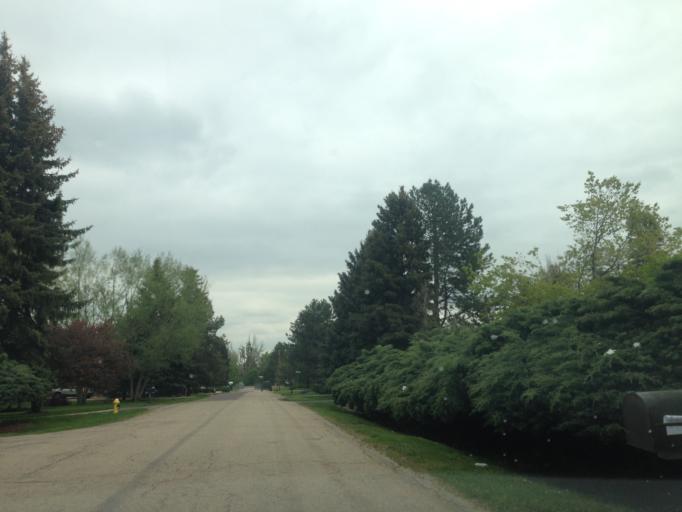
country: US
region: Colorado
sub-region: Boulder County
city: Louisville
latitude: 40.0013
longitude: -105.1713
